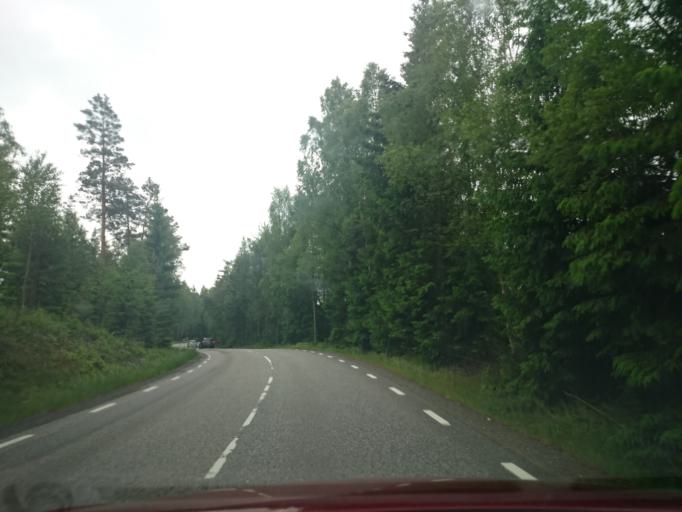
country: SE
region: Vaestra Goetaland
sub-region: Harryda Kommun
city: Hindas
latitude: 57.7076
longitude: 12.3517
